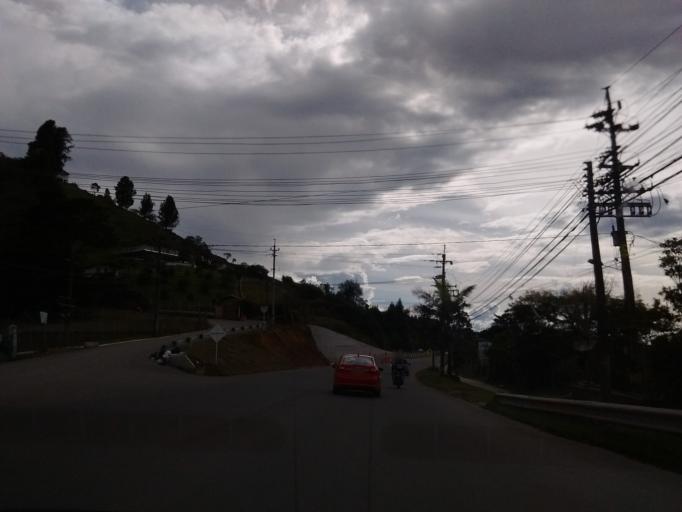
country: CO
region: Antioquia
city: Santuario
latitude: 6.1349
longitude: -75.2703
